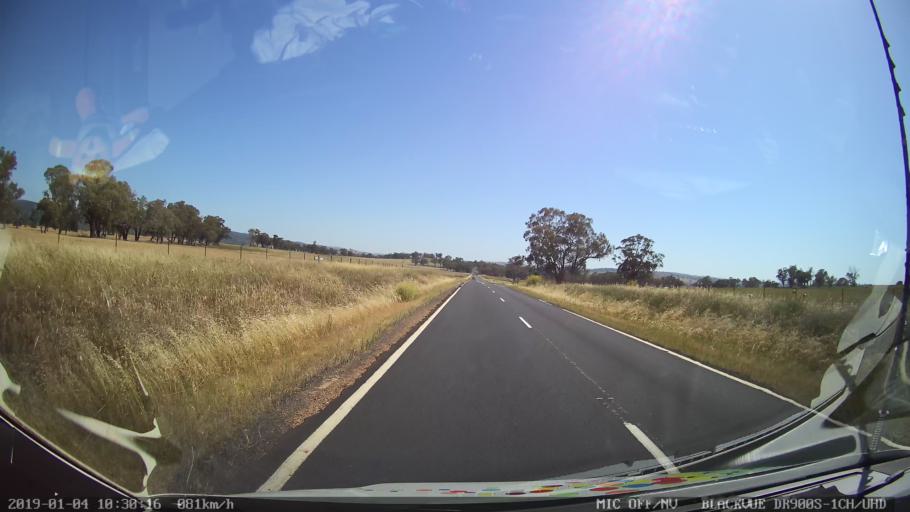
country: AU
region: New South Wales
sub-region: Cabonne
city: Canowindra
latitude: -33.3477
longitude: 148.6269
